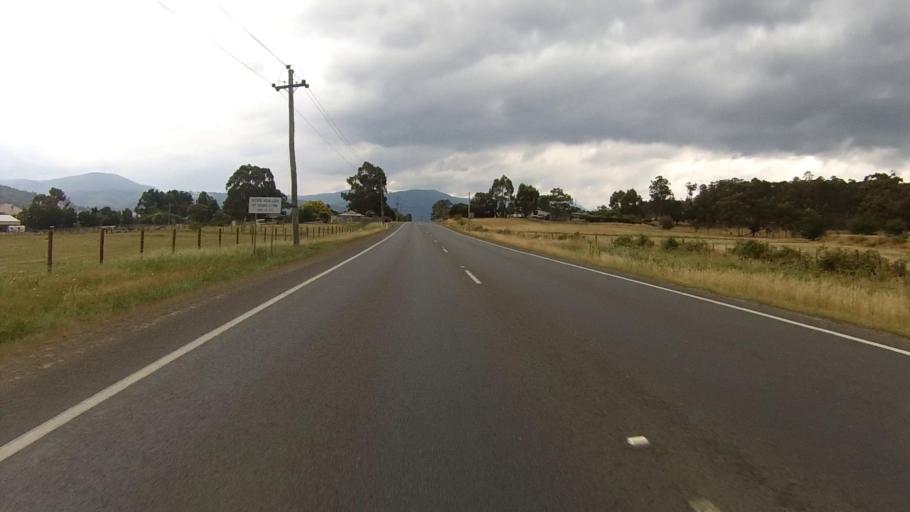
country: AU
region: Tasmania
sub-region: Huon Valley
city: Huonville
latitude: -43.0083
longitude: 147.0666
